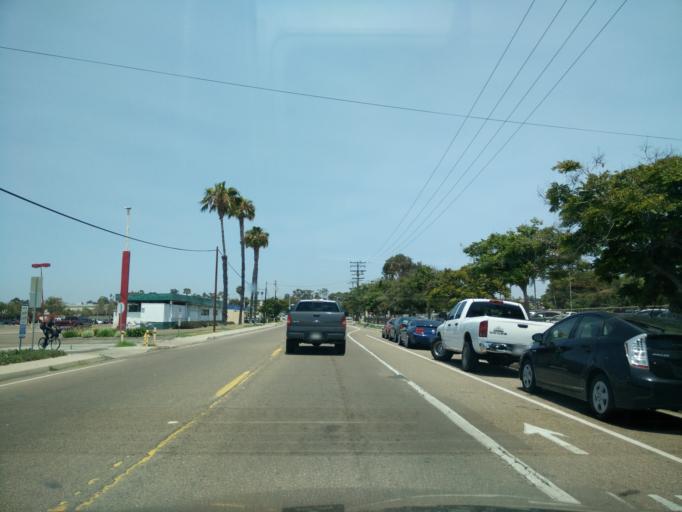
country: US
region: California
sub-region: San Diego County
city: Chula Vista
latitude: 32.6499
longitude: -117.0904
